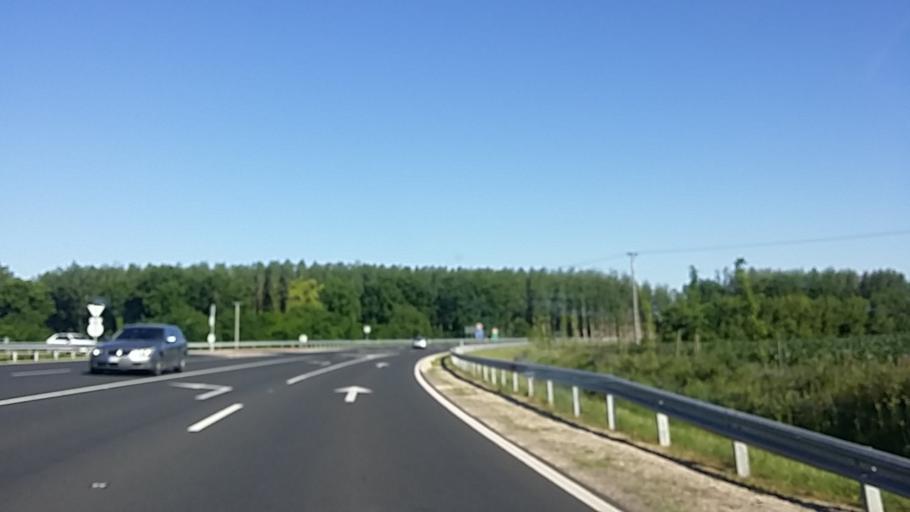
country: HU
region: Zala
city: Heviz
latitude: 46.7623
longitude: 17.1900
